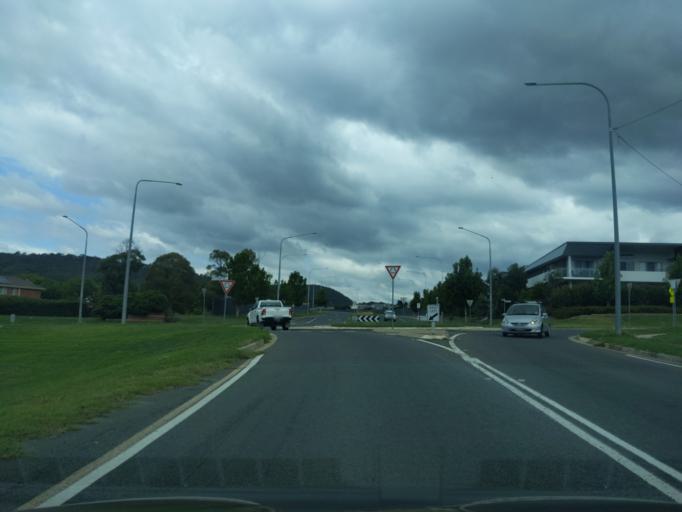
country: AU
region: New South Wales
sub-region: Queanbeyan
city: Queanbeyan
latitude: -35.3504
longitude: 149.2466
